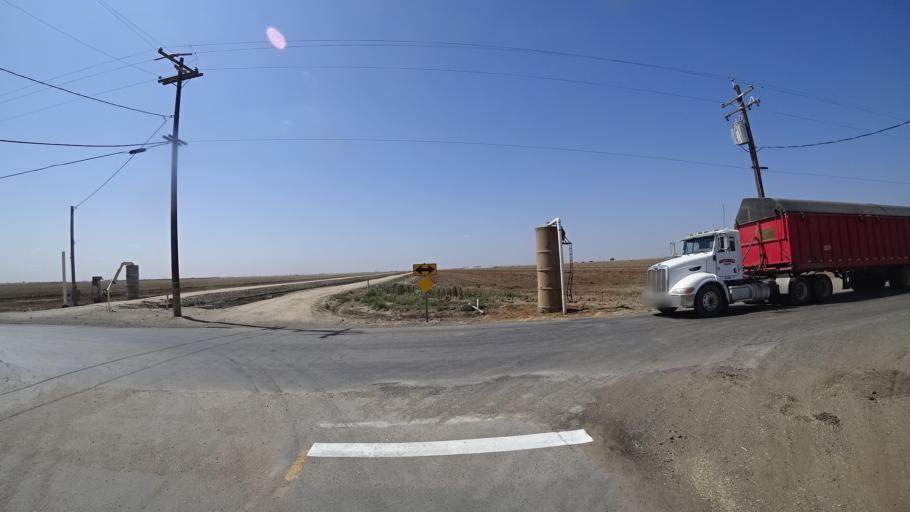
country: US
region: California
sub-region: Kings County
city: Home Garden
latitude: 36.1968
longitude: -119.6370
